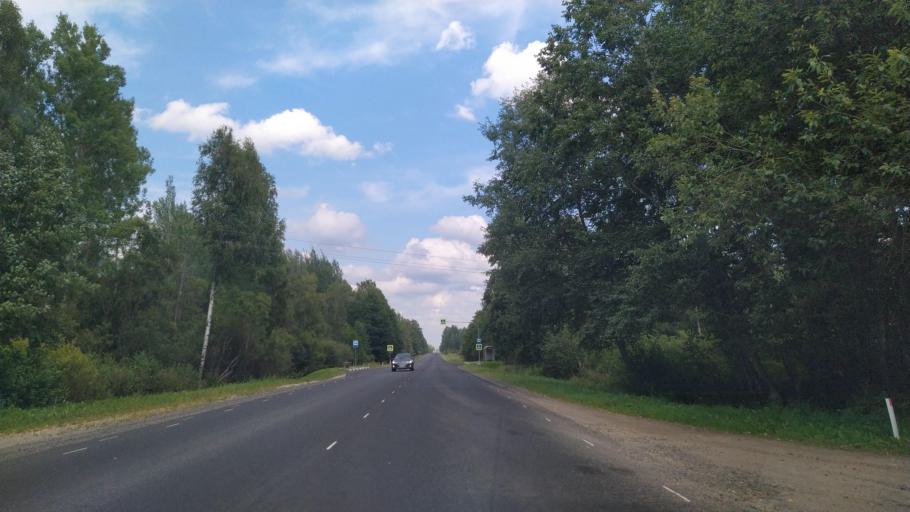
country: RU
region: Pskov
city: Porkhov
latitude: 57.7475
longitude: 29.4907
